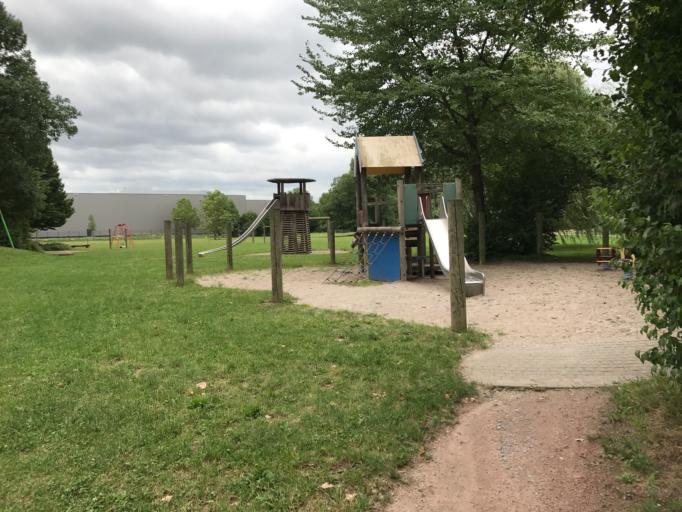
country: DE
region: Baden-Wuerttemberg
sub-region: Karlsruhe Region
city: Karlsruhe
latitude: 49.0274
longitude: 8.4583
